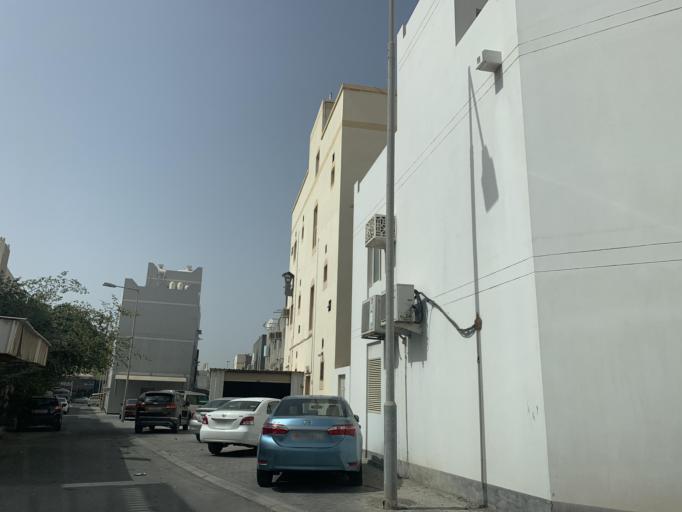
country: BH
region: Northern
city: Madinat `Isa
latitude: 26.1555
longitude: 50.5145
